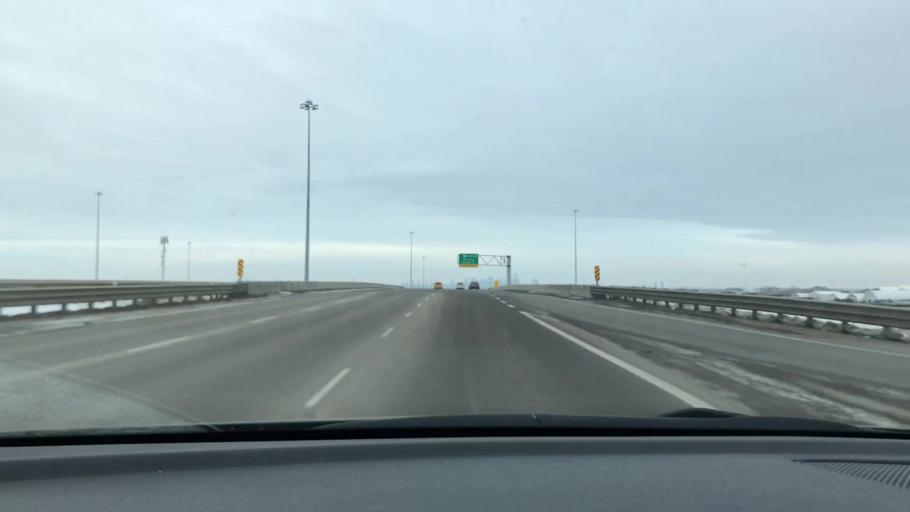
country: CA
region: Alberta
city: Sherwood Park
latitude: 53.5128
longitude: -113.3424
